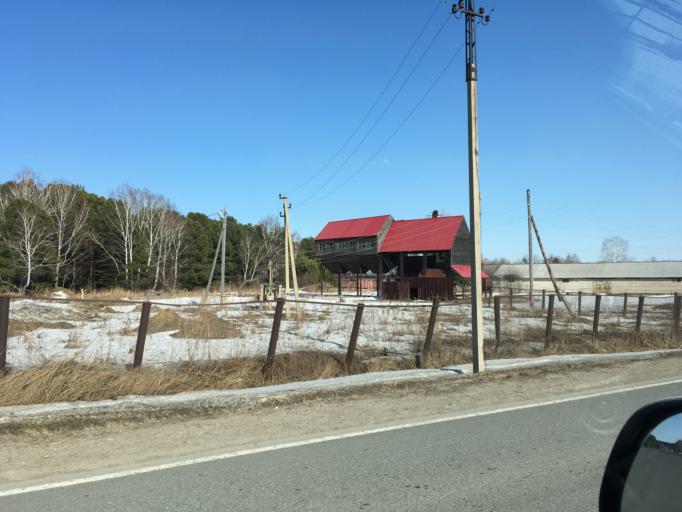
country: RU
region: Tomsk
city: Moryakovskiy Zaton
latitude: 56.5874
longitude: 84.6327
